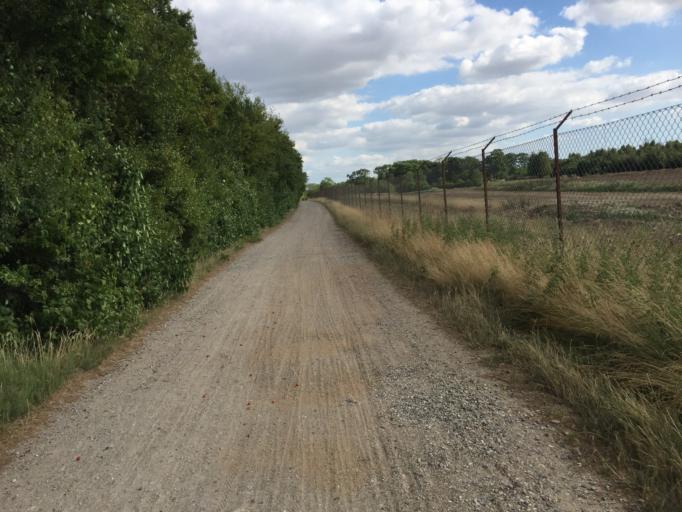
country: DK
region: South Denmark
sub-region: Odense Kommune
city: Neder Holluf
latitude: 55.3597
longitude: 10.4350
